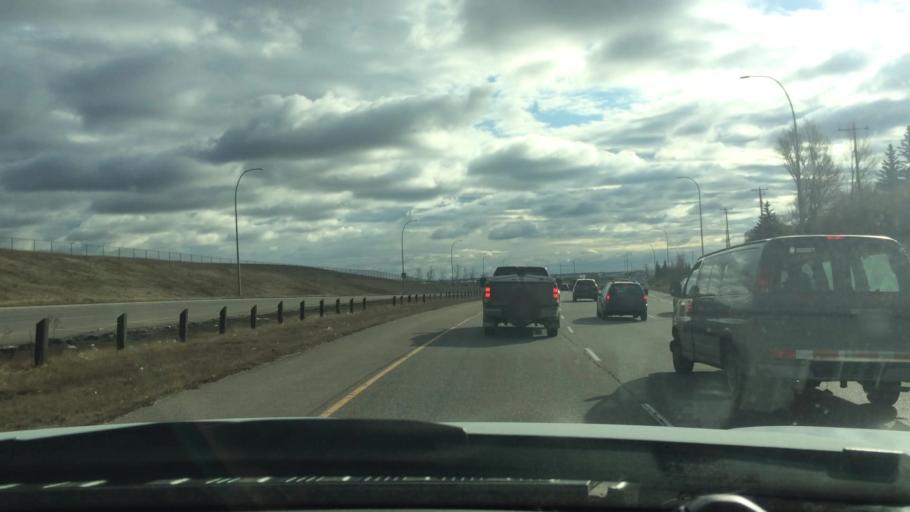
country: CA
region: Alberta
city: Calgary
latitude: 51.1299
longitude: -114.0572
